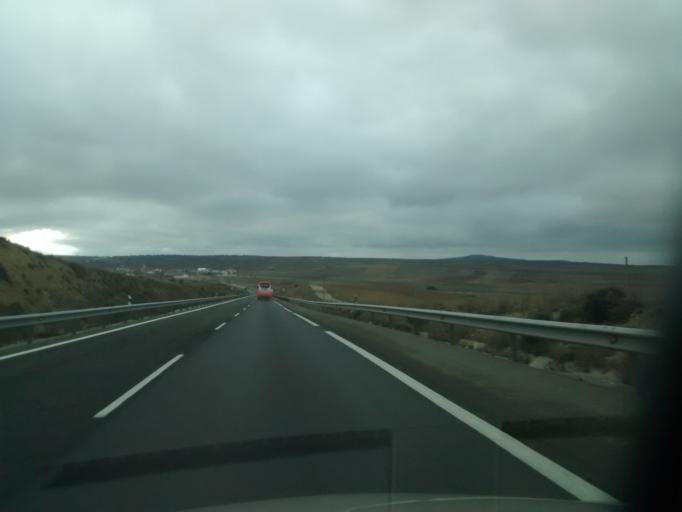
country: ES
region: Castille-La Mancha
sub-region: Provincia de Guadalajara
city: Torremocha del Campo
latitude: 40.9901
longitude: -2.5996
